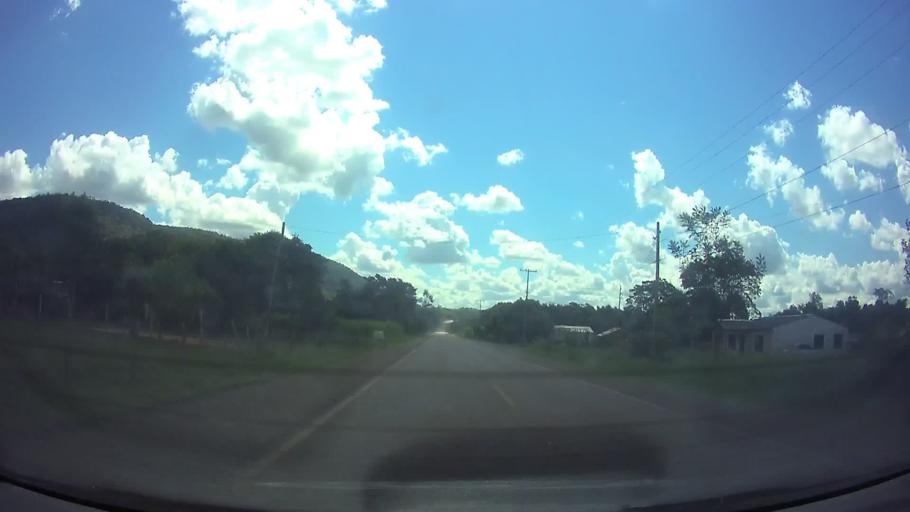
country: PY
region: Paraguari
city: La Colmena
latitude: -25.9182
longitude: -56.7293
